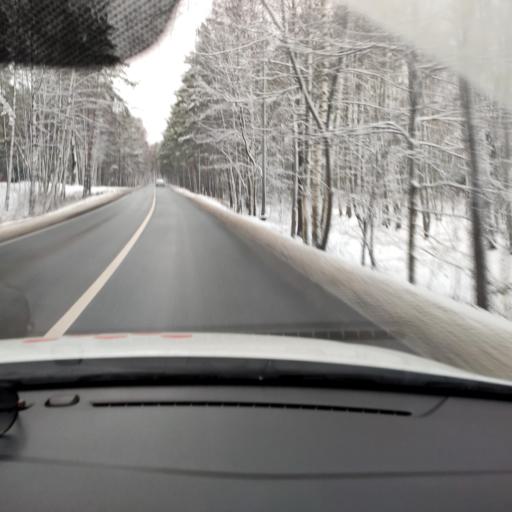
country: RU
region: Tatarstan
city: Verkhniy Uslon
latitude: 55.6308
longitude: 49.0165
